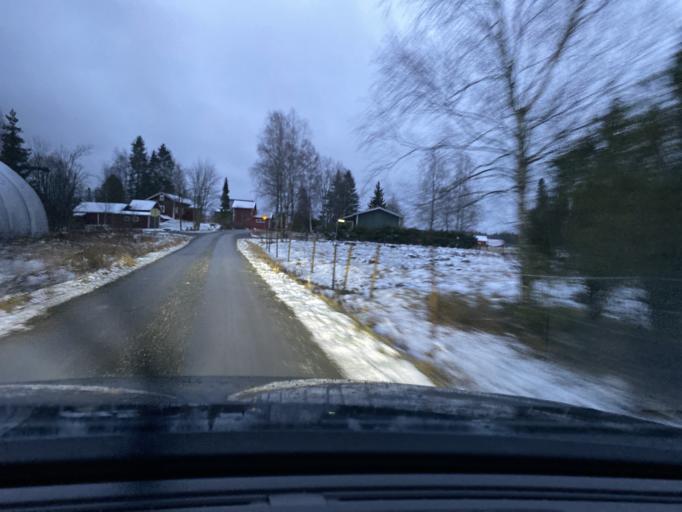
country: FI
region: Pirkanmaa
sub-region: Lounais-Pirkanmaa
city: Punkalaidun
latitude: 61.1180
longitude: 23.0293
